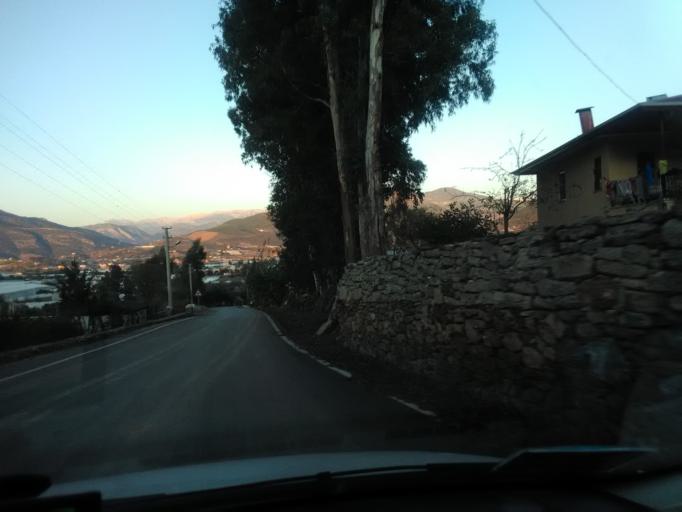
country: TR
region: Antalya
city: Gazipasa
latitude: 36.2474
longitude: 32.3402
